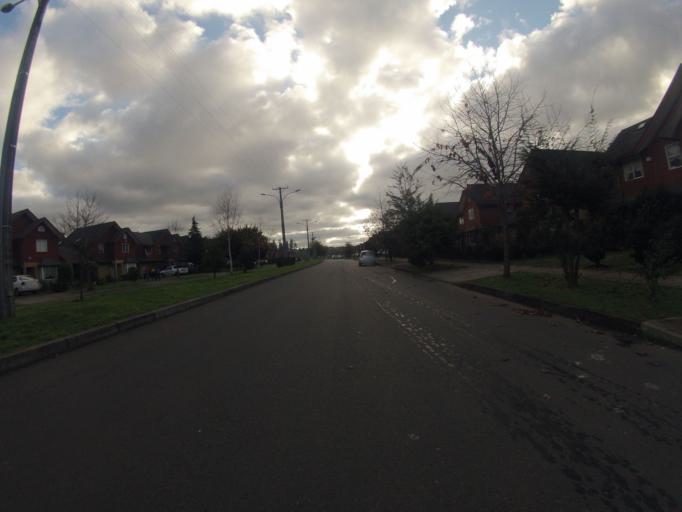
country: CL
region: Araucania
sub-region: Provincia de Cautin
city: Temuco
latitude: -38.7403
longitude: -72.6461
